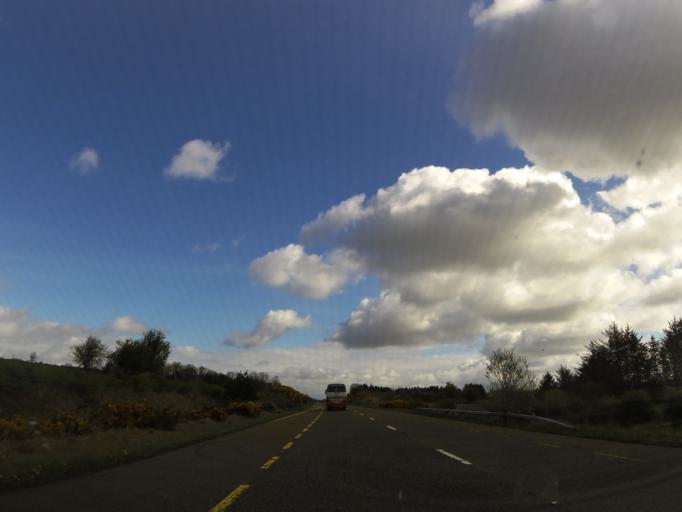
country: IE
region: Connaught
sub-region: Maigh Eo
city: Kiltamagh
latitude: 53.8130
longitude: -8.8990
